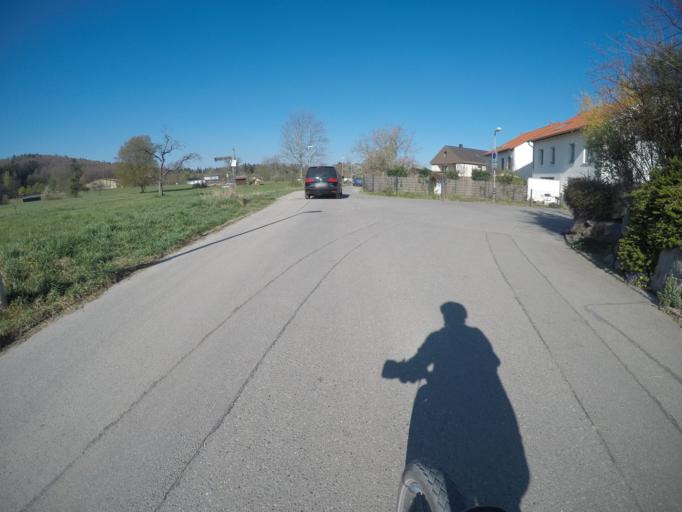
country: DE
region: Baden-Wuerttemberg
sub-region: Tuebingen Region
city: Dettenhausen
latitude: 48.6001
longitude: 9.1025
